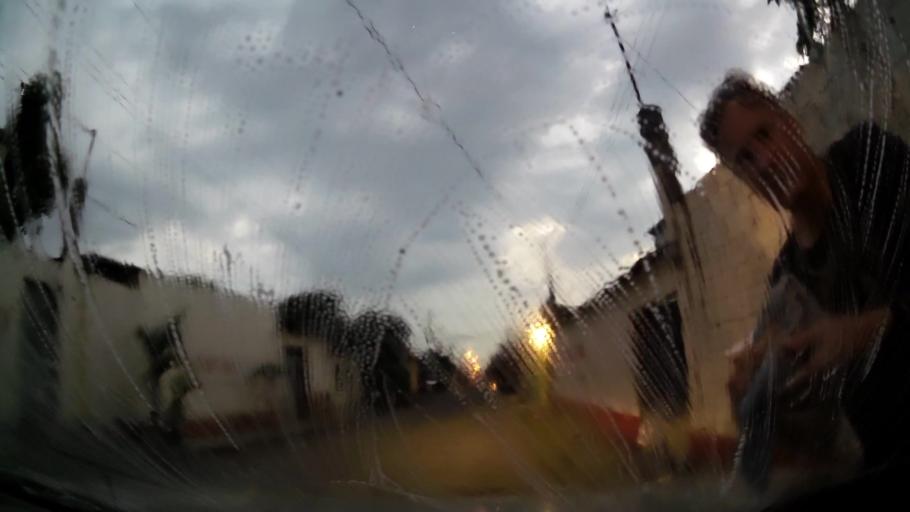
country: GT
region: Escuintla
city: Santa Lucia Cotzumalguapa
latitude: 14.3419
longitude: -91.0270
